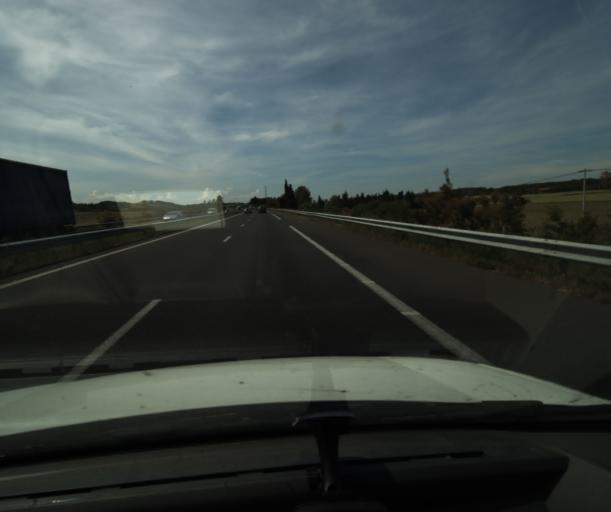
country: FR
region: Languedoc-Roussillon
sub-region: Departement de l'Aude
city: Villeneuve-la-Comptal
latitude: 43.3177
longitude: 1.8779
